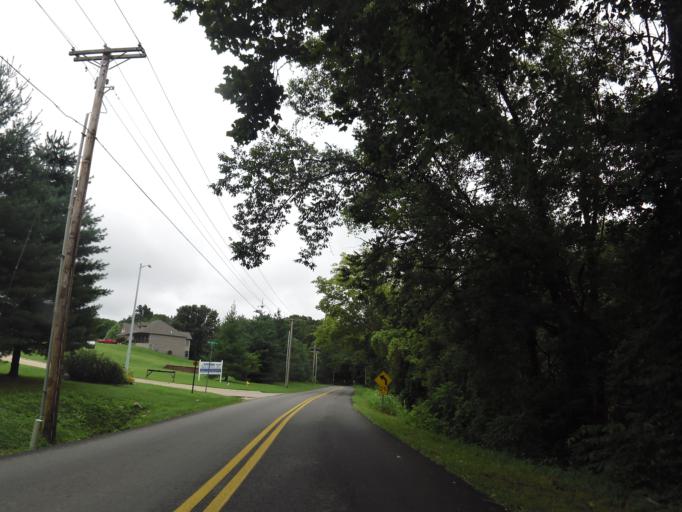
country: US
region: Missouri
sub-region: Cape Girardeau County
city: Cape Girardeau
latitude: 37.3567
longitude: -89.5631
